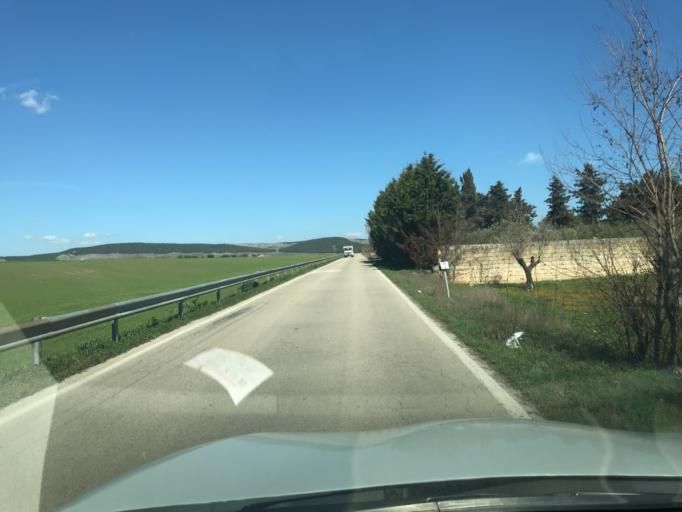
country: IT
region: Apulia
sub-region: Provincia di Bari
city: Gravina in Puglia
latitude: 40.8488
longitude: 16.4278
